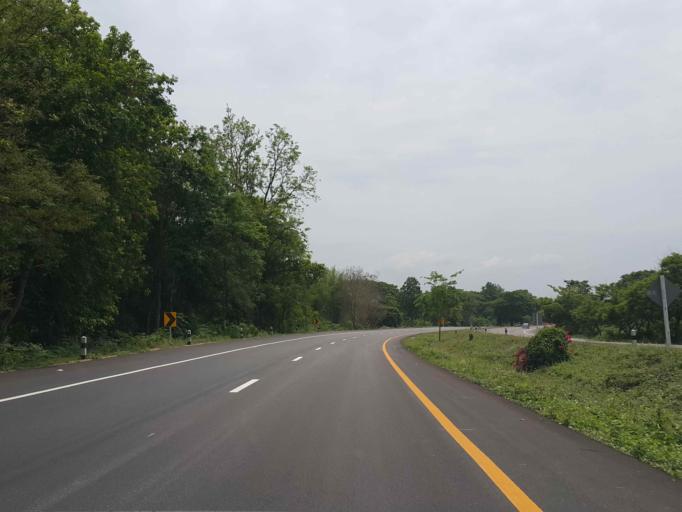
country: TH
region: Lampang
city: Sop Prap
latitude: 17.9188
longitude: 99.3449
